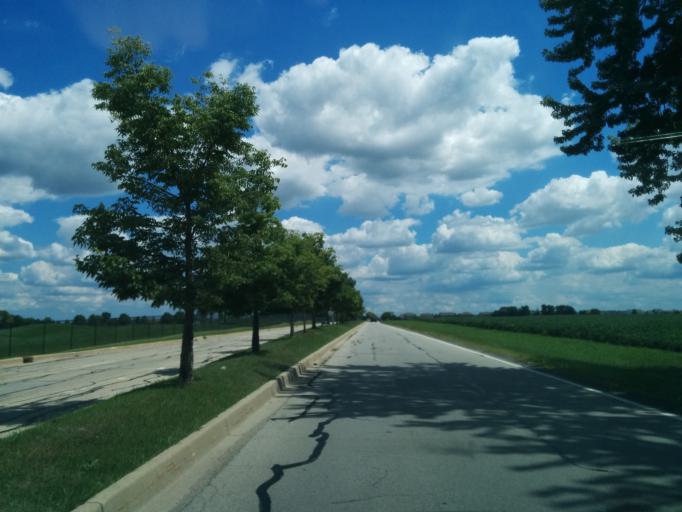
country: US
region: Illinois
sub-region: Will County
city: Plainfield
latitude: 41.6814
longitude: -88.1651
